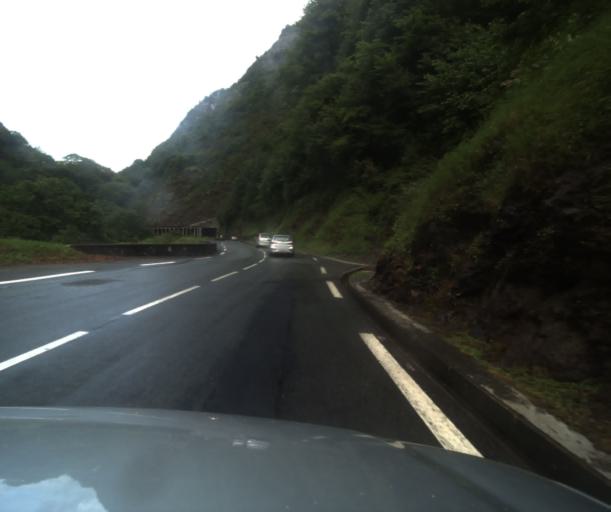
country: FR
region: Midi-Pyrenees
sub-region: Departement des Hautes-Pyrenees
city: Pierrefitte-Nestalas
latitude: 42.9268
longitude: -0.0417
